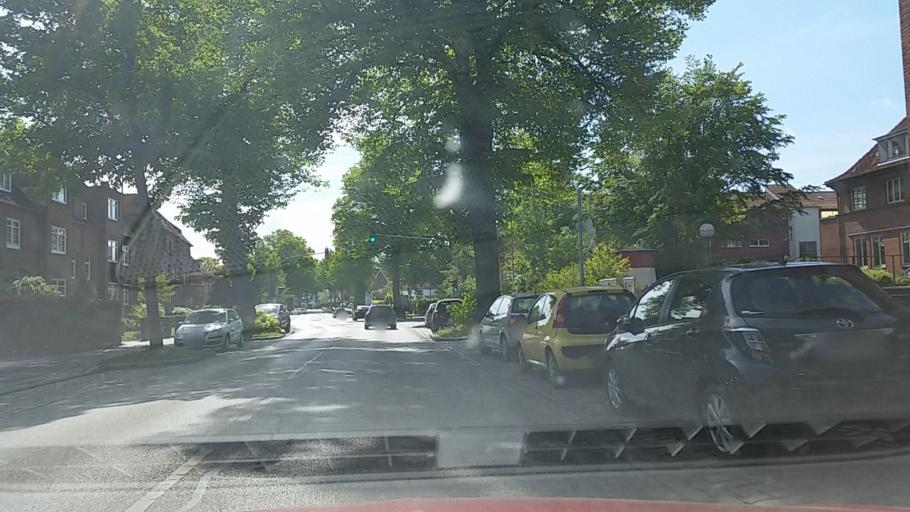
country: DE
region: Schleswig-Holstein
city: Luebeck
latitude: 53.8542
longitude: 10.6644
